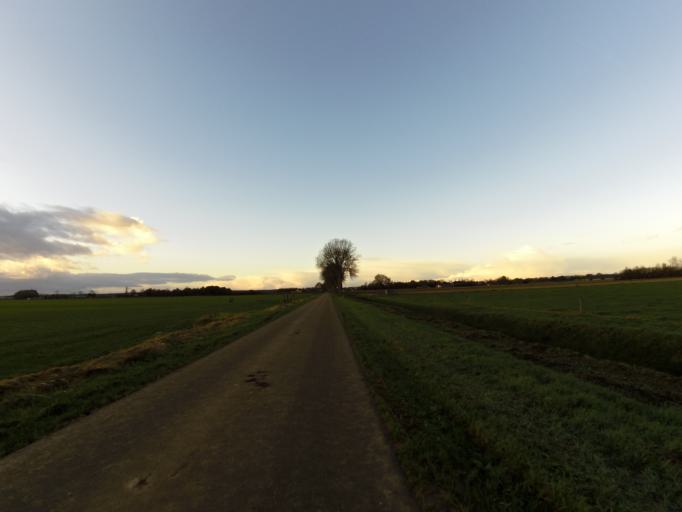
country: NL
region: Gelderland
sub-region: Oude IJsselstreek
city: Gendringen
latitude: 51.8747
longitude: 6.3203
